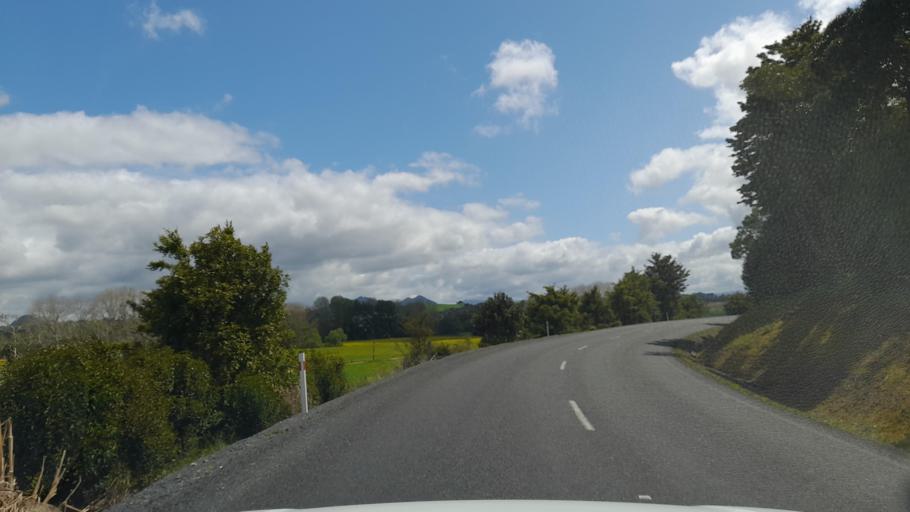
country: NZ
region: Northland
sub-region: Whangarei
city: Maungatapere
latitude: -35.7113
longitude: 174.0535
